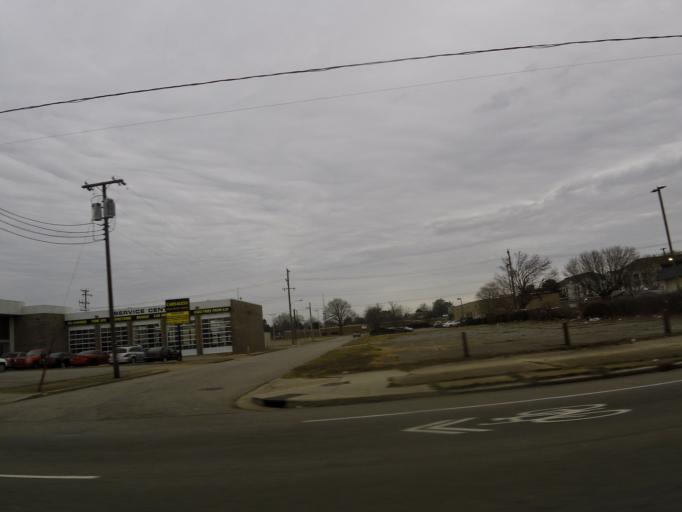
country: US
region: Virginia
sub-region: City of Portsmouth
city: Portsmouth
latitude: 36.8350
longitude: -76.3141
